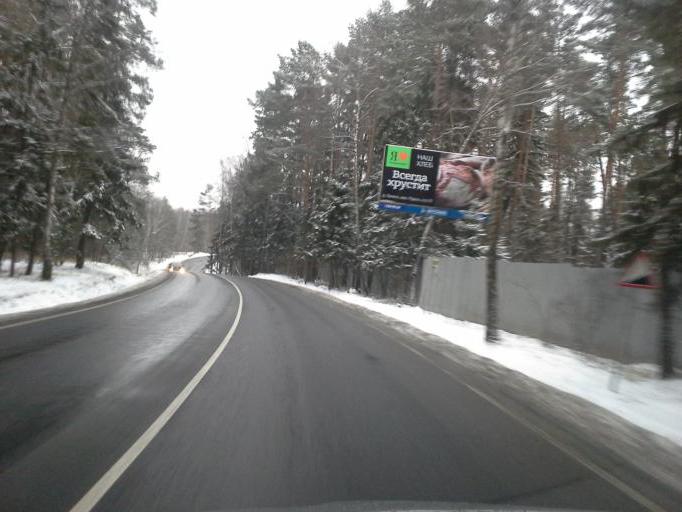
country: RU
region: Moskovskaya
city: Nikolina Gora
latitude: 55.7078
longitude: 37.0910
